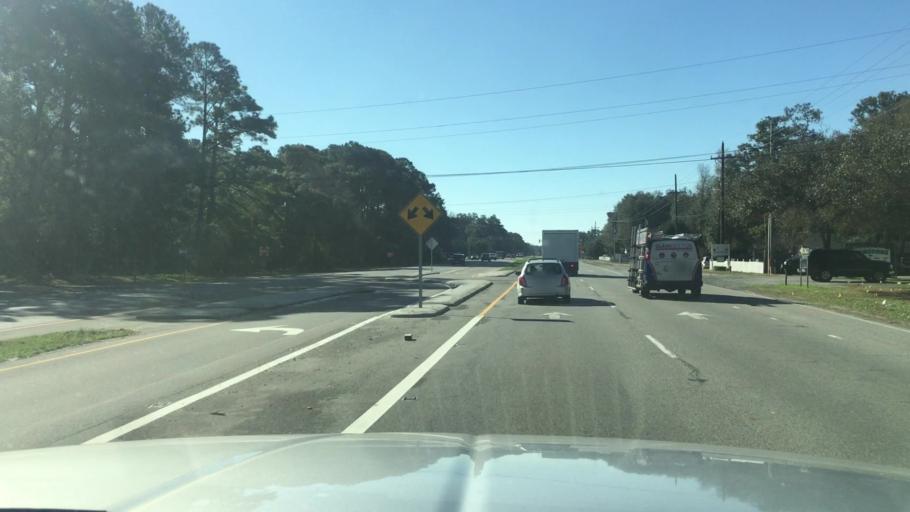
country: US
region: North Carolina
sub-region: New Hanover County
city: Sea Breeze
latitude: 34.0918
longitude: -77.8971
